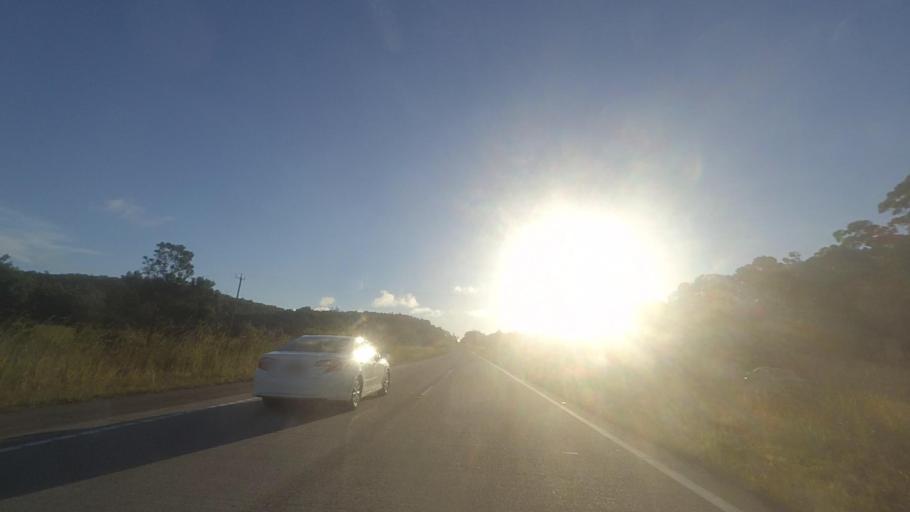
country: AU
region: New South Wales
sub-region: Great Lakes
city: Bulahdelah
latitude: -32.5304
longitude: 152.1860
